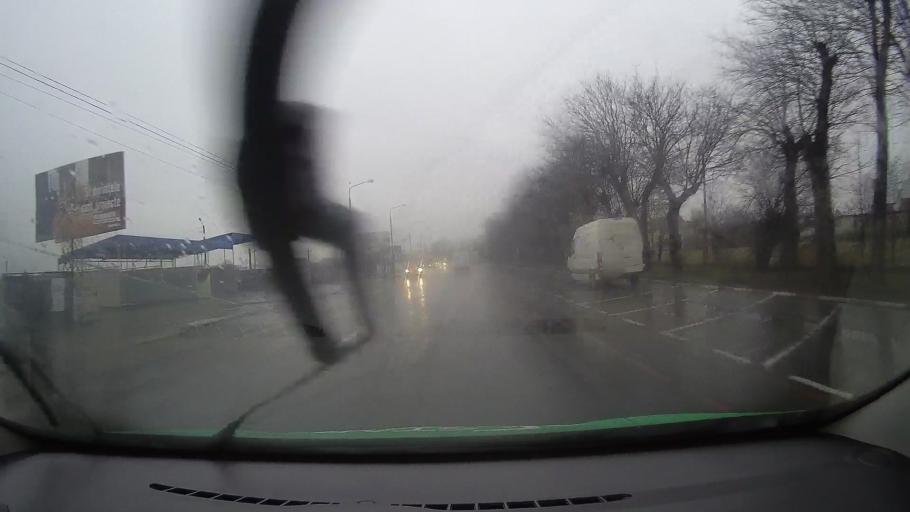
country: RO
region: Sibiu
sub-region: Municipiul Sibiu
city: Sibiu
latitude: 45.8173
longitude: 24.1497
